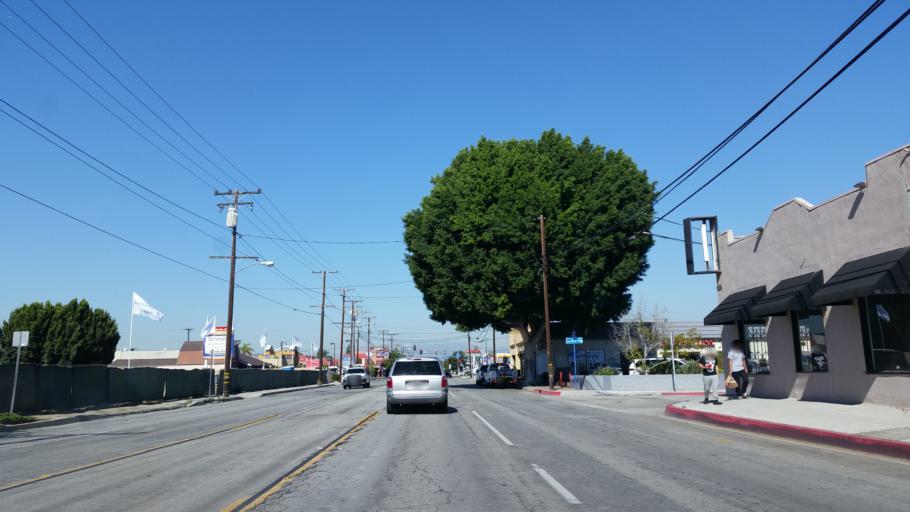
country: US
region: California
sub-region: Los Angeles County
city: Cerritos
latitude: 33.8568
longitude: -118.0723
